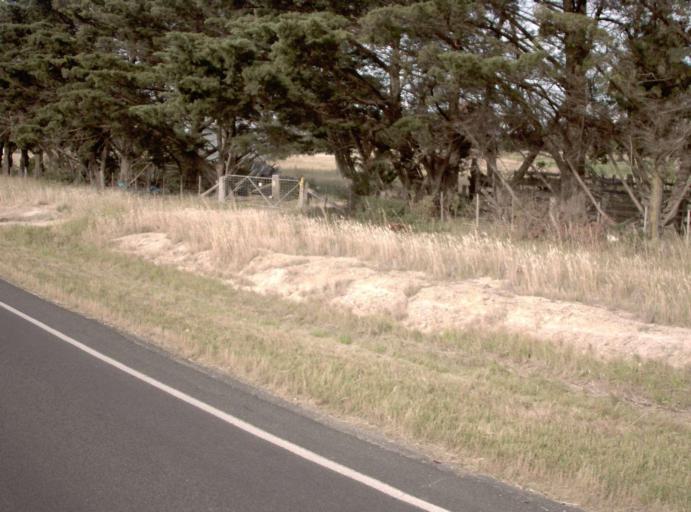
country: AU
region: Victoria
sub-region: Wellington
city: Heyfield
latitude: -38.0135
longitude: 146.6714
